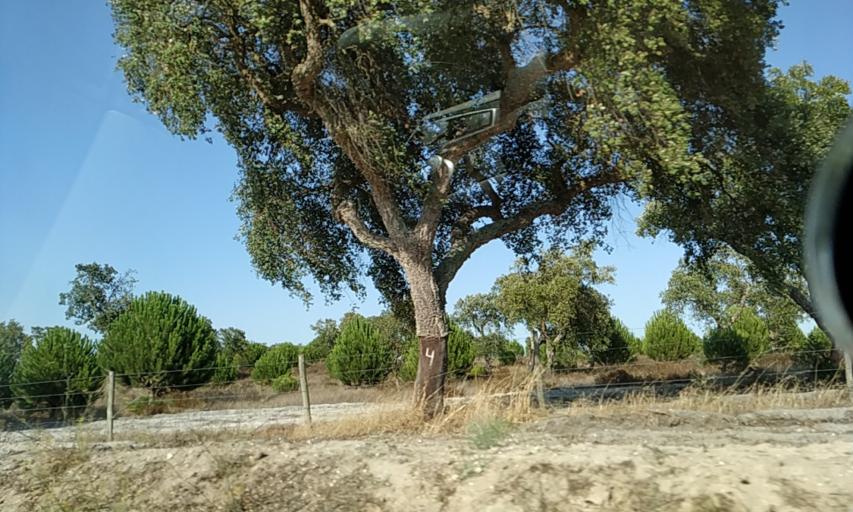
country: PT
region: Santarem
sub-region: Coruche
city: Coruche
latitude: 39.0370
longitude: -8.5606
